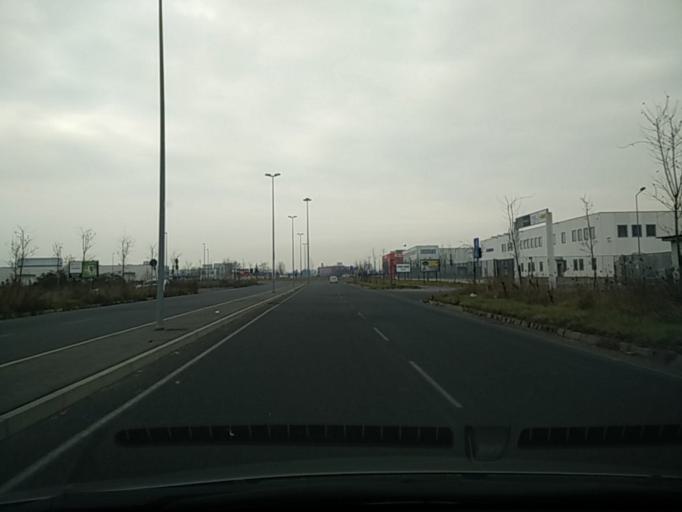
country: IT
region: Piedmont
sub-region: Provincia di Torino
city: Settimo Torinese
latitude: 45.1448
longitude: 7.7395
